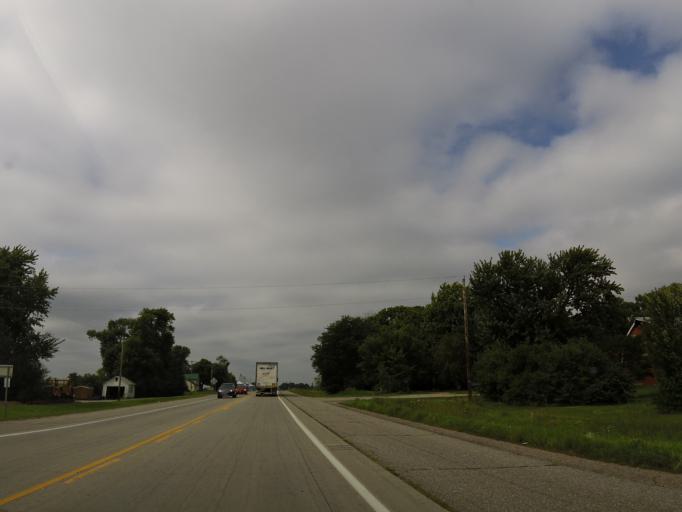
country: US
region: Minnesota
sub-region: Renville County
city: Bird Island
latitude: 44.7675
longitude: -94.9086
